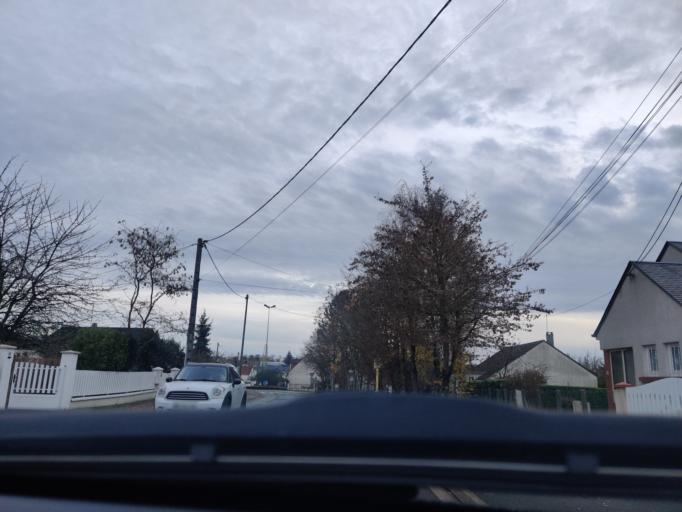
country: FR
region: Centre
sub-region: Departement du Loiret
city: La Chapelle-Saint-Mesmin
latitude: 47.8898
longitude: 1.8290
